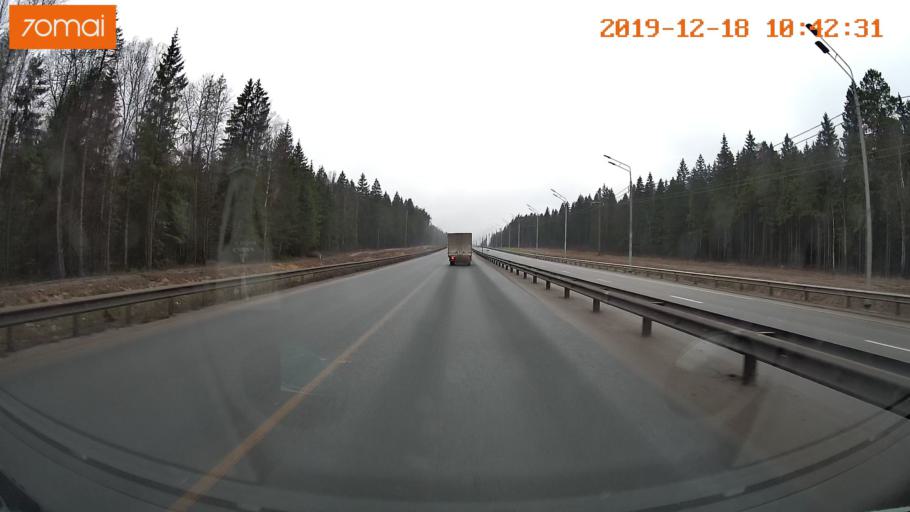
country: RU
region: Moskovskaya
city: Aprelevka
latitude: 55.4622
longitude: 37.0967
